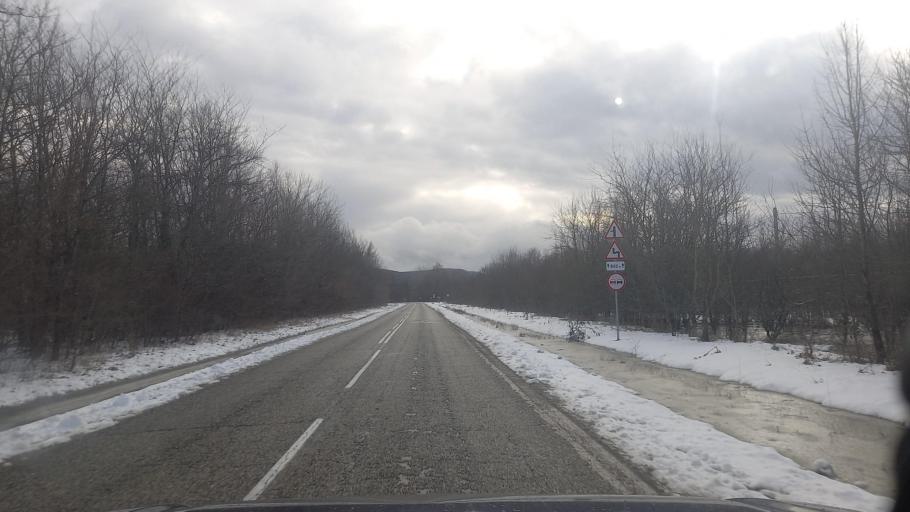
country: RU
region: Krasnodarskiy
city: Smolenskaya
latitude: 44.7641
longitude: 38.8470
